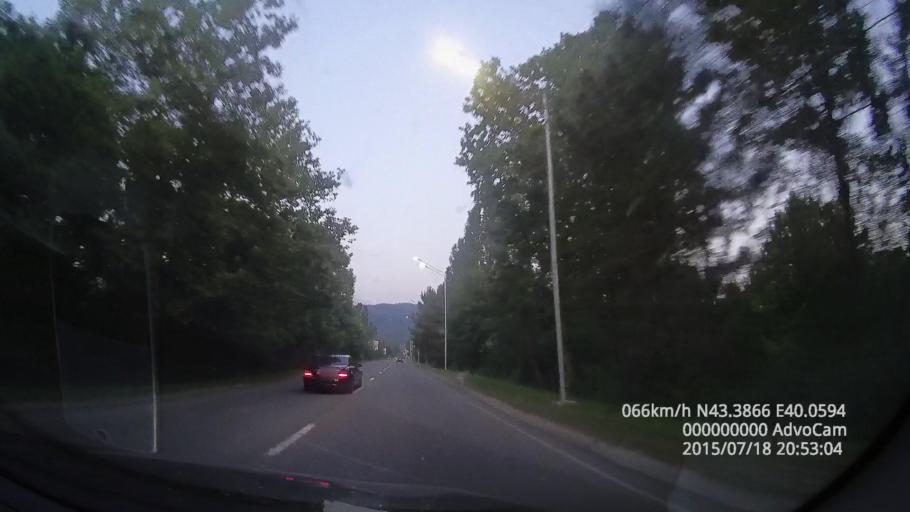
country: GE
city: Gantiadi
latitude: 43.3864
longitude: 40.0611
